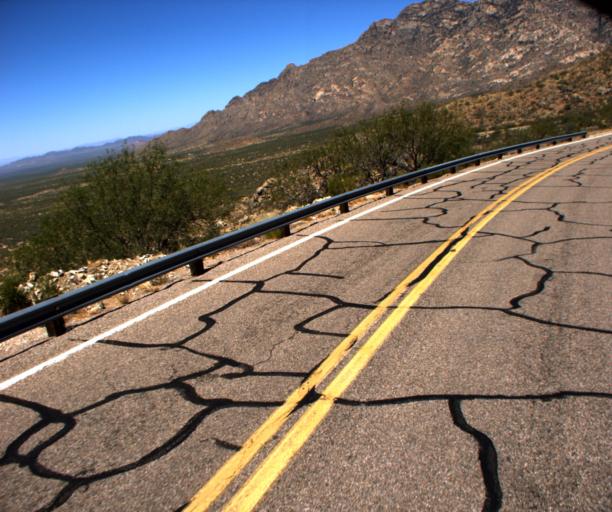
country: US
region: Arizona
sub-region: Pima County
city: Three Points
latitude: 31.9887
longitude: -111.5924
